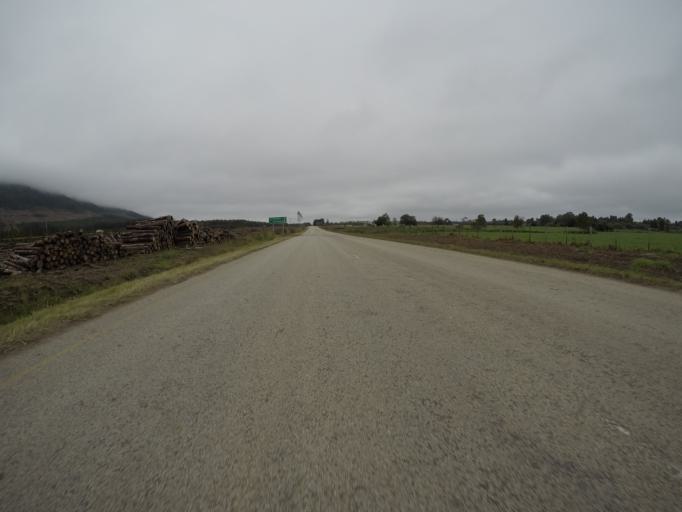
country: ZA
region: Eastern Cape
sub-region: Cacadu District Municipality
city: Kareedouw
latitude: -33.9859
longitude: 24.0669
